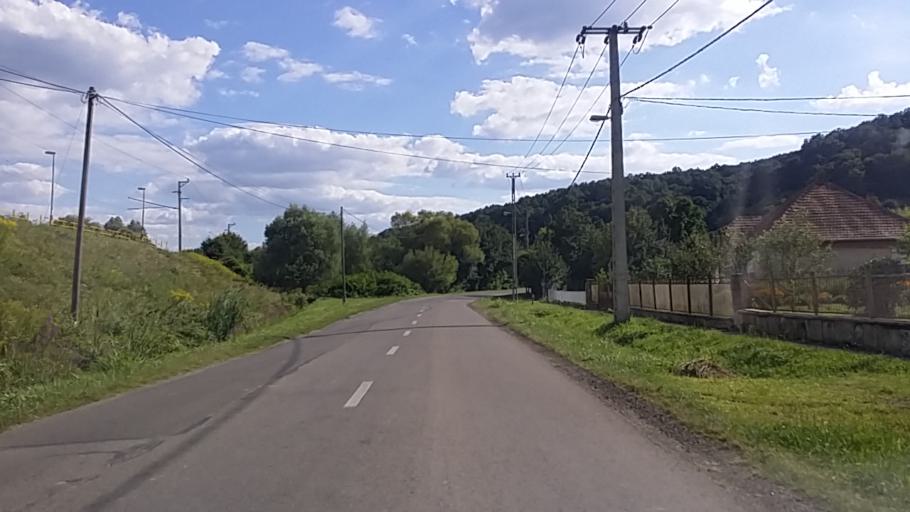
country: HU
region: Baranya
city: Sasd
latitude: 46.2021
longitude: 18.0834
